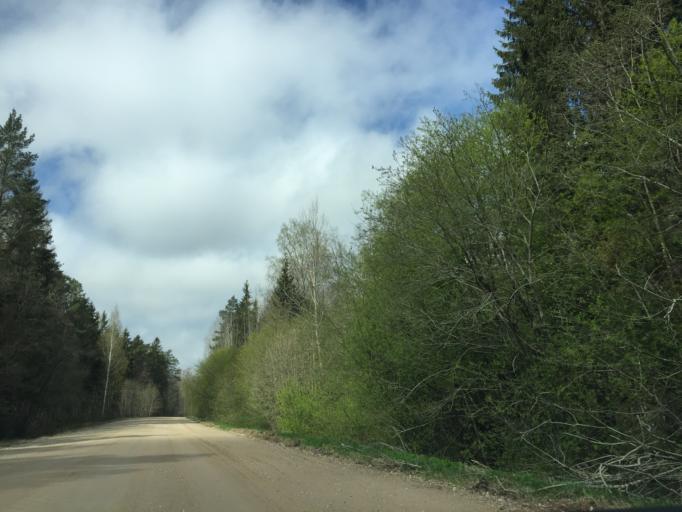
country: LV
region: Apes Novads
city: Ape
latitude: 57.4969
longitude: 26.4079
